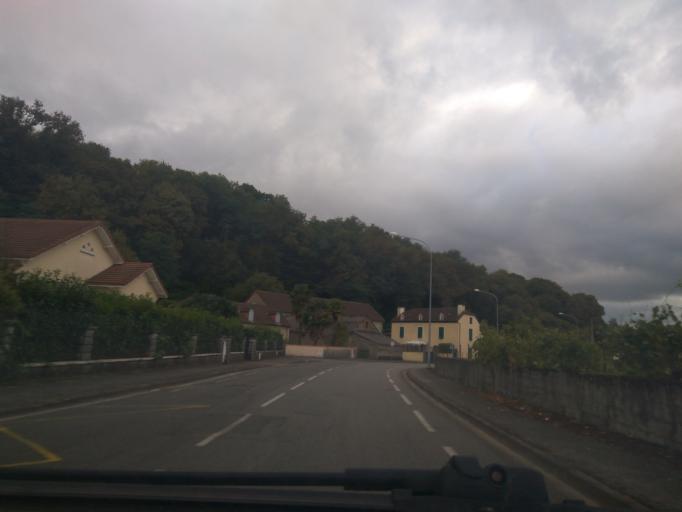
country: FR
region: Aquitaine
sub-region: Departement des Pyrenees-Atlantiques
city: Bizanos
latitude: 43.2883
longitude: -0.3443
